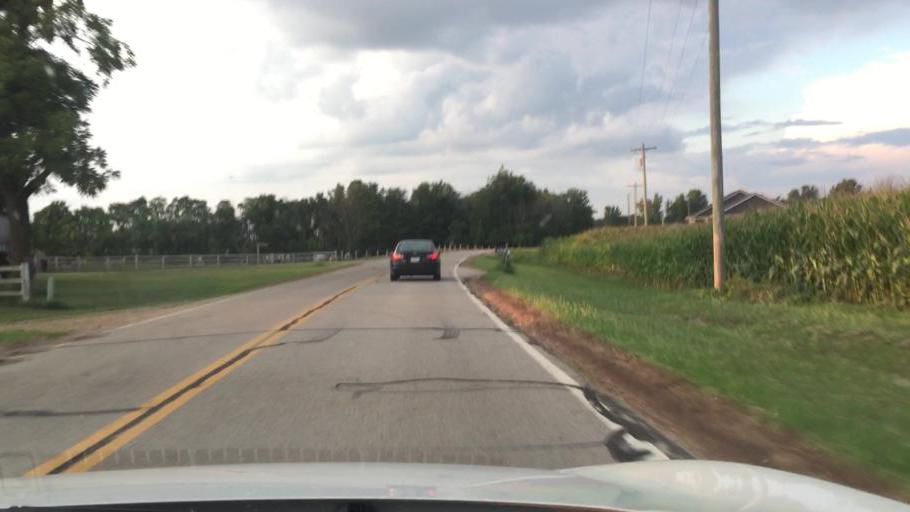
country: US
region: Ohio
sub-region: Champaign County
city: Mechanicsburg
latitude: 40.0394
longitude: -83.5685
